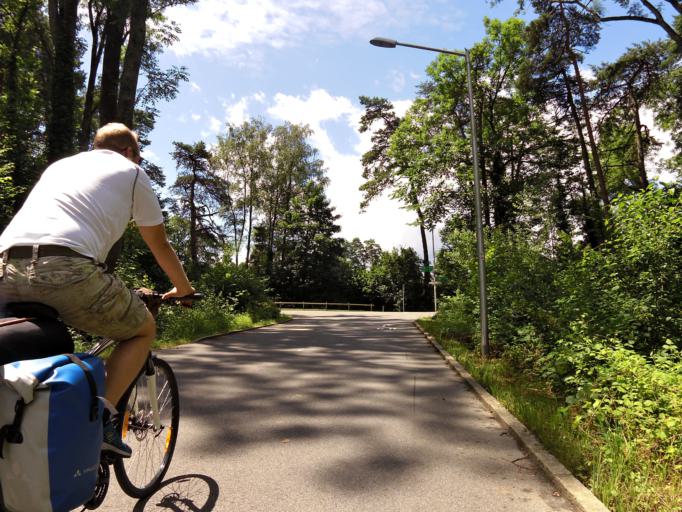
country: AT
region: Vorarlberg
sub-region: Politischer Bezirk Bregenz
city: Hard
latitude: 47.4962
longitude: 9.6994
